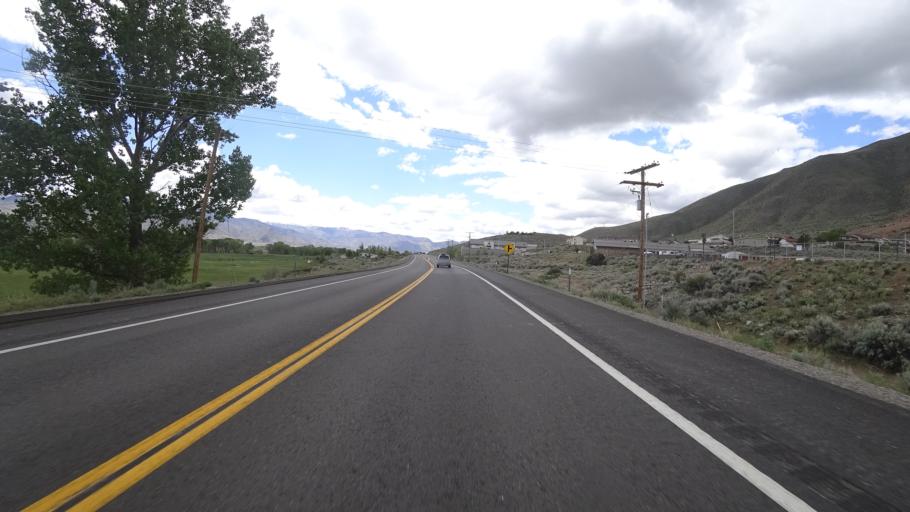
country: US
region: Nevada
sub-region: Lyon County
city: Smith Valley
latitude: 38.5896
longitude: -119.5161
